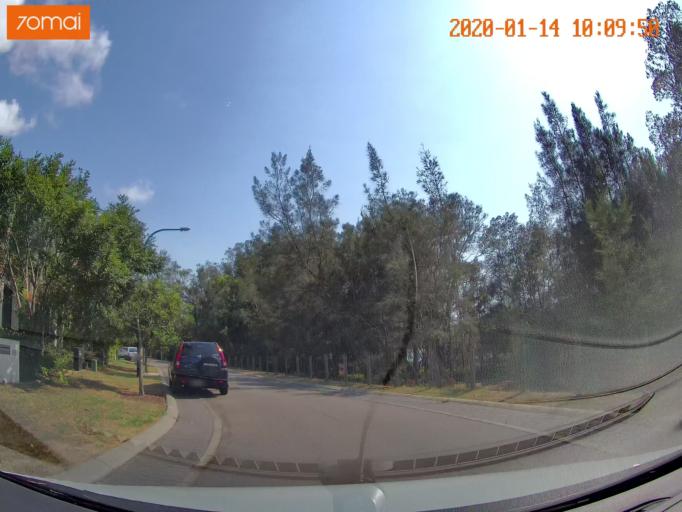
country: AU
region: New South Wales
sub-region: Wyong Shire
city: Kingfisher Shores
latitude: -33.1235
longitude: 151.5378
